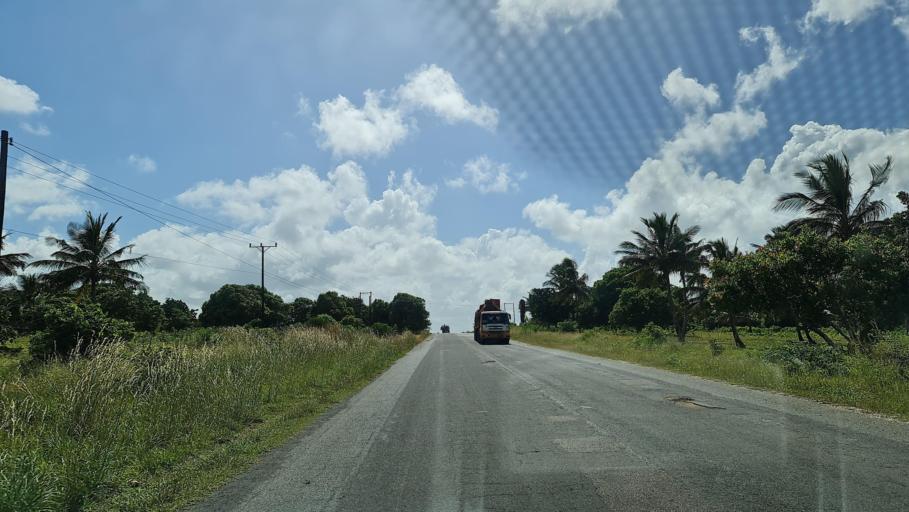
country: MZ
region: Gaza
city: Manjacaze
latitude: -24.6777
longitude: 34.5606
